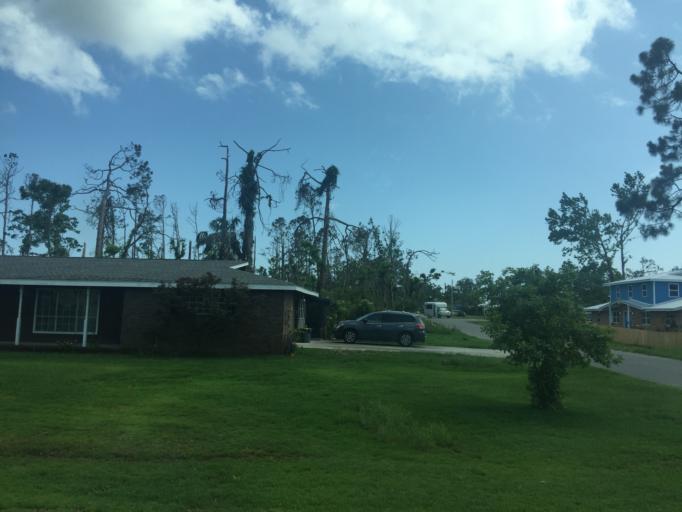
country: US
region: Florida
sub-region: Bay County
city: Pretty Bayou
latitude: 30.1968
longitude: -85.7095
